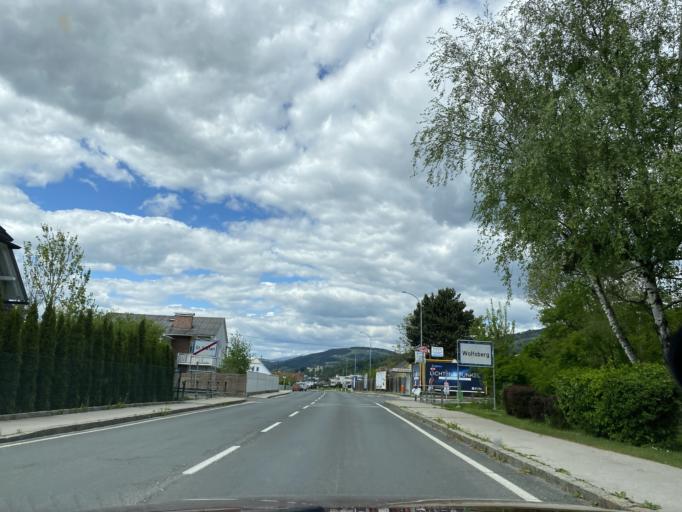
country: AT
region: Carinthia
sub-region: Politischer Bezirk Wolfsberg
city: Wolfsberg
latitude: 46.8150
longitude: 14.8507
